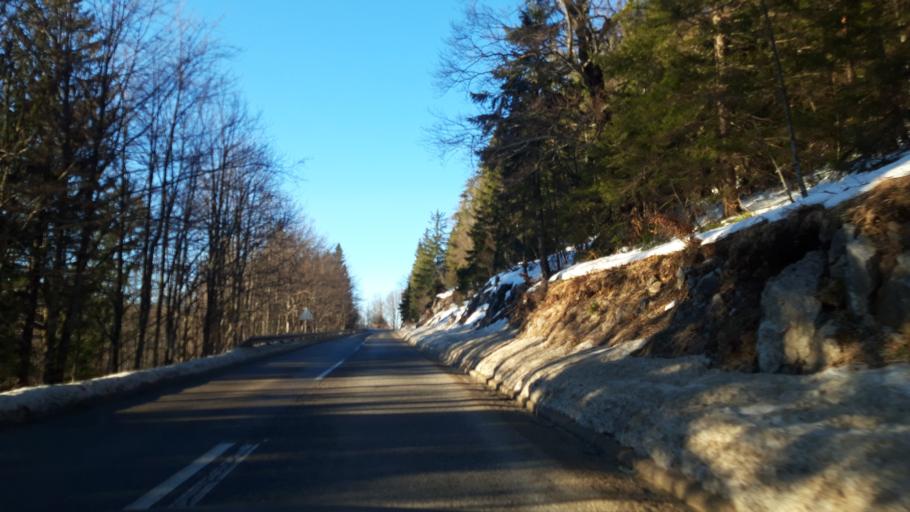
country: BA
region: Republika Srpska
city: Vlasenica
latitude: 44.1389
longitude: 18.9513
